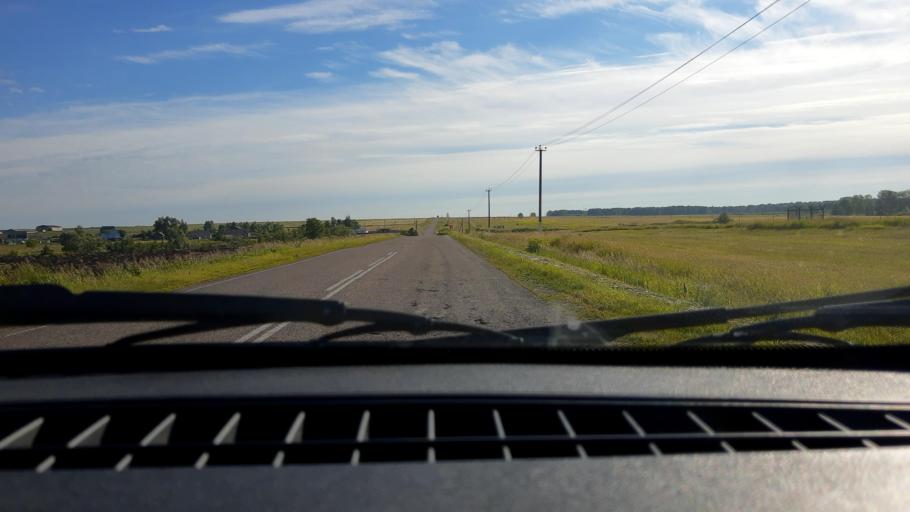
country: RU
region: Bashkortostan
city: Asanovo
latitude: 54.7795
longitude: 55.5002
